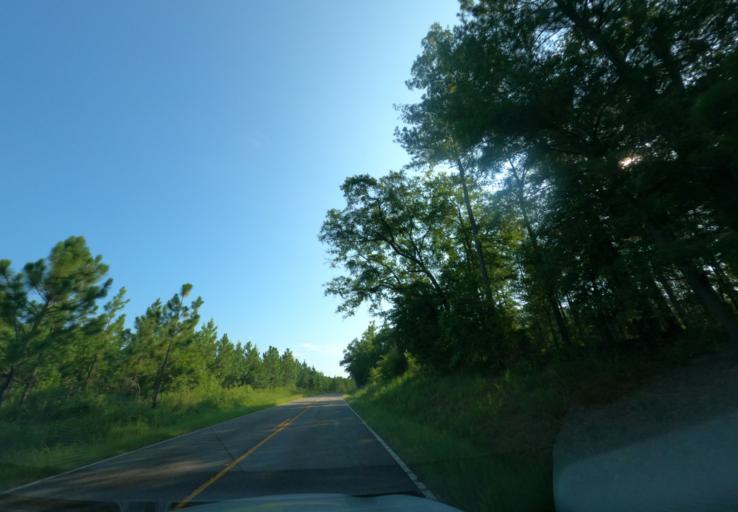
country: US
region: South Carolina
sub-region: Edgefield County
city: Edgefield
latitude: 33.7542
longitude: -81.9564
